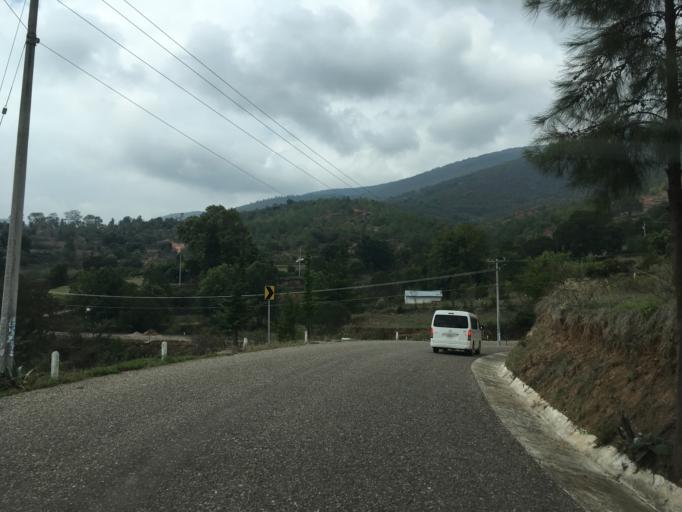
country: MX
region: Oaxaca
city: Santiago Tilantongo
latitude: 17.2462
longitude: -97.3098
